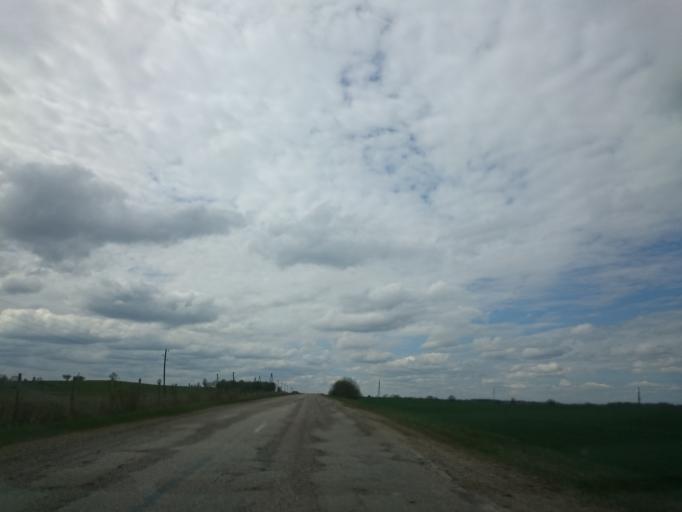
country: LV
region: Jaunpils
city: Jaunpils
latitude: 56.9090
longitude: 22.9476
